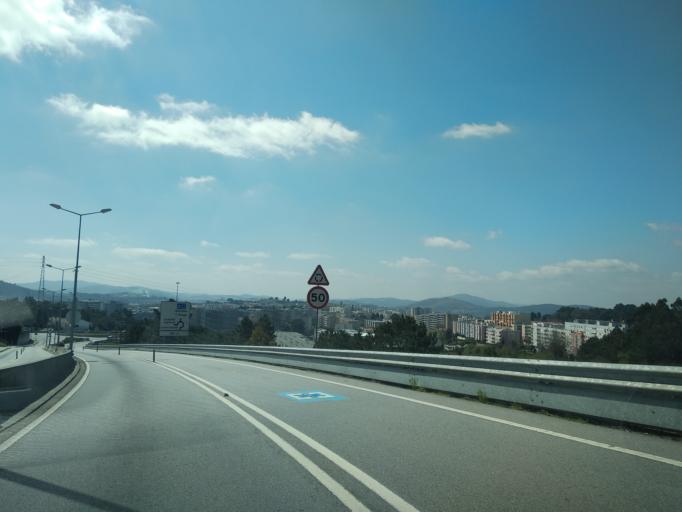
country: PT
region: Braga
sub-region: Braga
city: Adaufe
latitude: 41.5683
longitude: -8.4028
